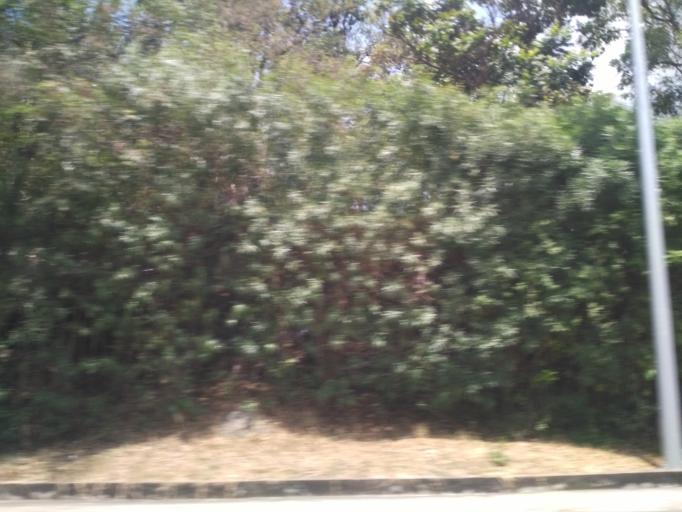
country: TZ
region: Mwanza
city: Mwanza
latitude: -2.5228
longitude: 32.8917
